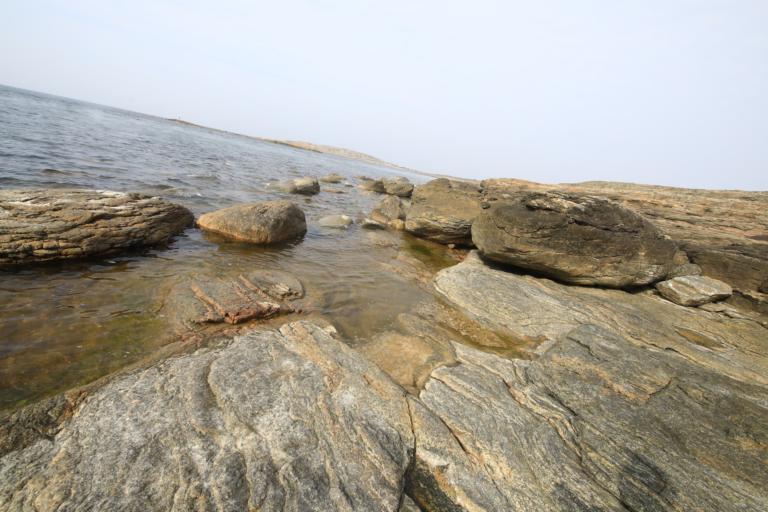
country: SE
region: Halland
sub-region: Kungsbacka Kommun
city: Frillesas
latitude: 57.2499
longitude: 12.0909
